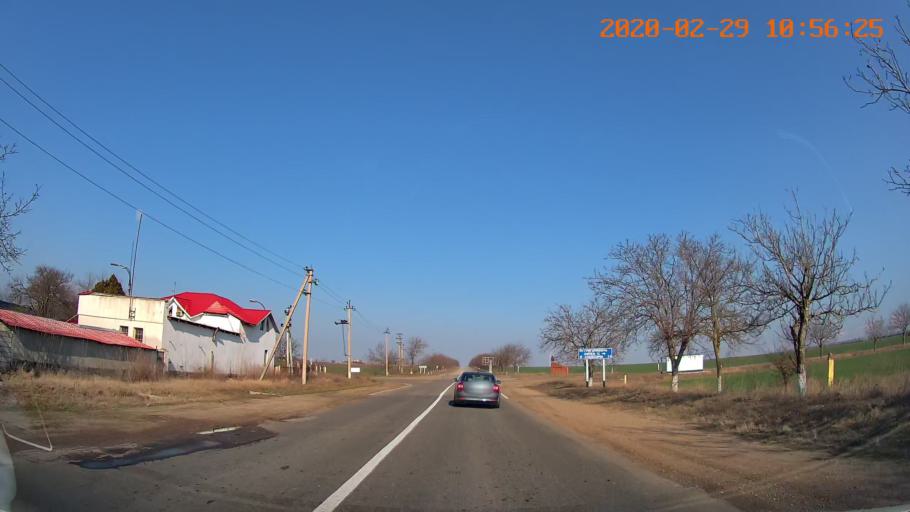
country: MD
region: Telenesti
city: Grigoriopol
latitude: 47.1457
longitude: 29.3245
